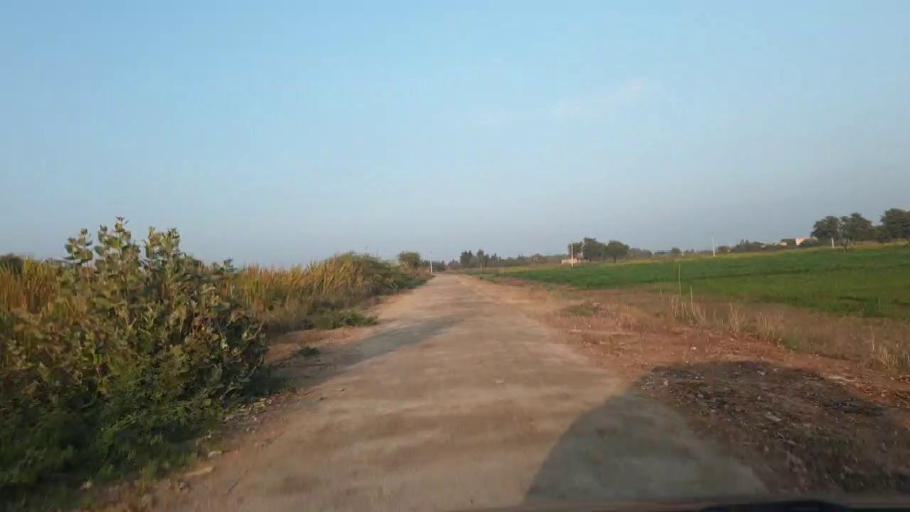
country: PK
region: Sindh
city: Berani
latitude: 25.8388
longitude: 68.7288
